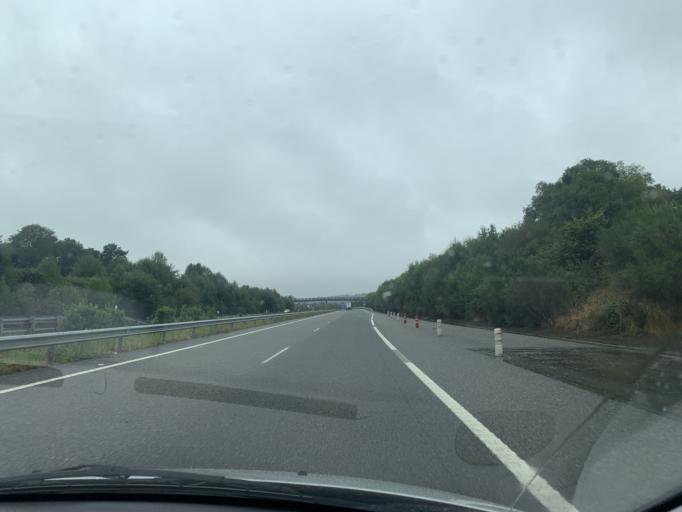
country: ES
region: Galicia
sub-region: Provincia de Lugo
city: Vilalba
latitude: 43.3212
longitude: -7.6730
